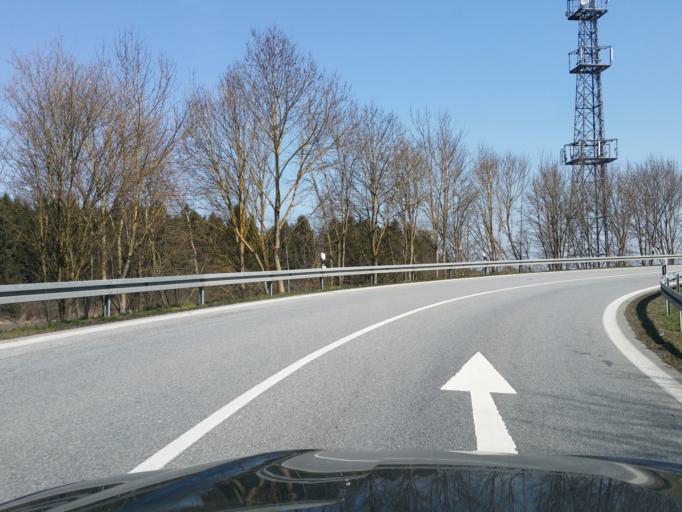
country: DE
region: Bavaria
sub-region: Upper Bavaria
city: Langenbach
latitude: 48.3975
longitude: 11.8553
